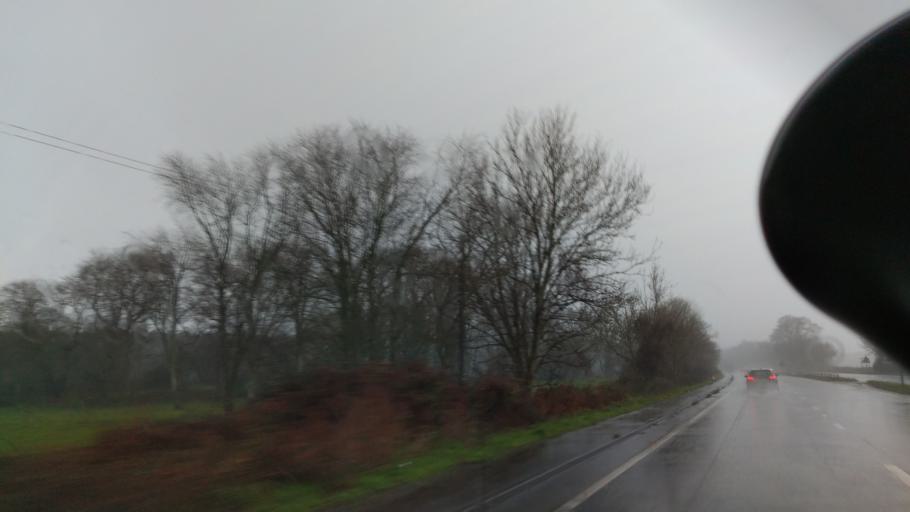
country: GB
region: England
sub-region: West Sussex
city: Arundel
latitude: 50.8573
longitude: -0.5846
